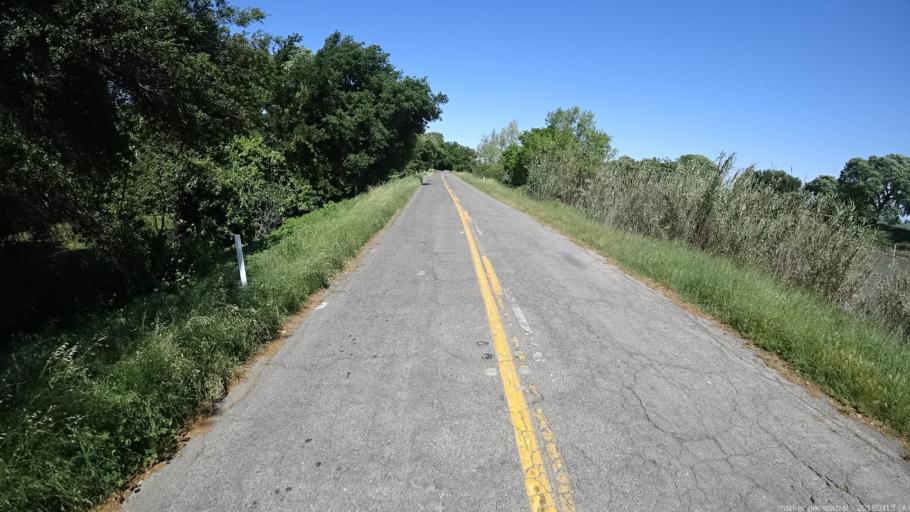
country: US
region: California
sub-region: Sacramento County
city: Walnut Grove
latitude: 38.2951
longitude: -121.5831
